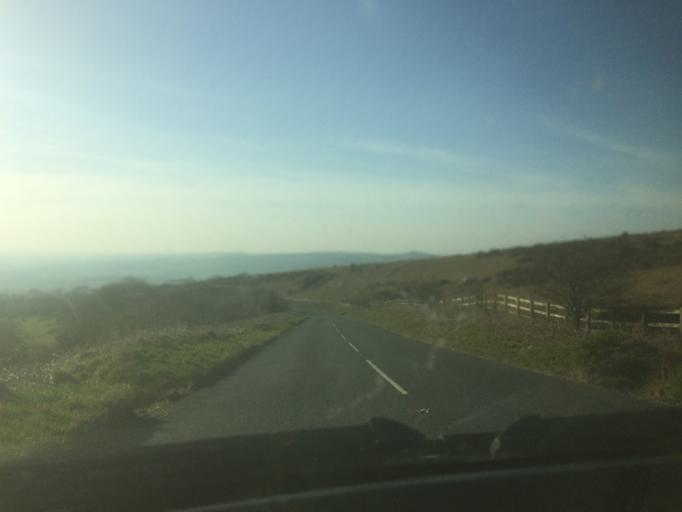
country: GB
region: England
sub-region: Devon
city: Horrabridge
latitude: 50.5583
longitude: -4.0796
